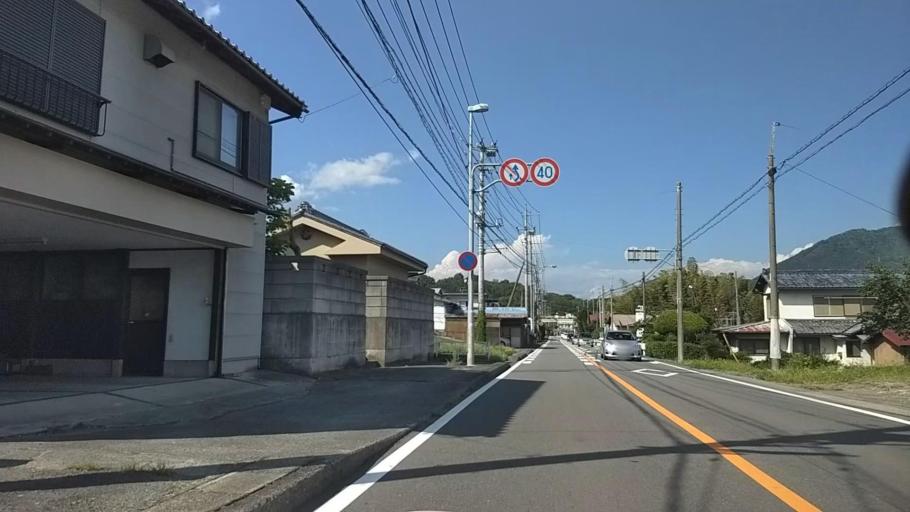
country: JP
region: Yamanashi
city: Ryuo
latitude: 35.4109
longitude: 138.4422
